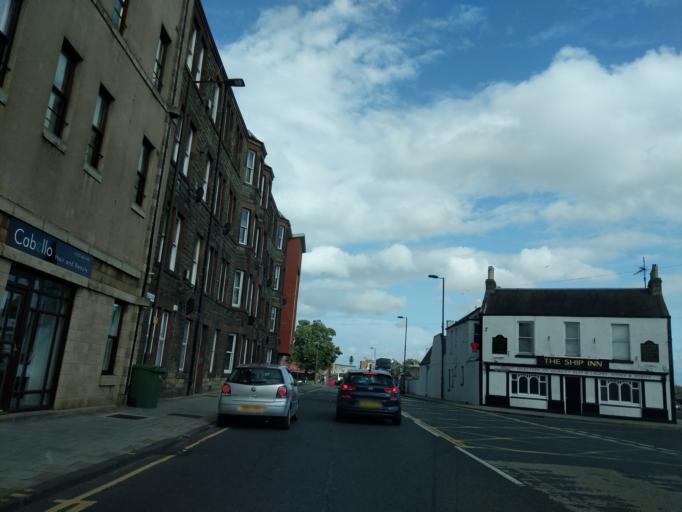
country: GB
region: Scotland
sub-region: East Lothian
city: Musselburgh
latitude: 55.9440
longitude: -3.0668
